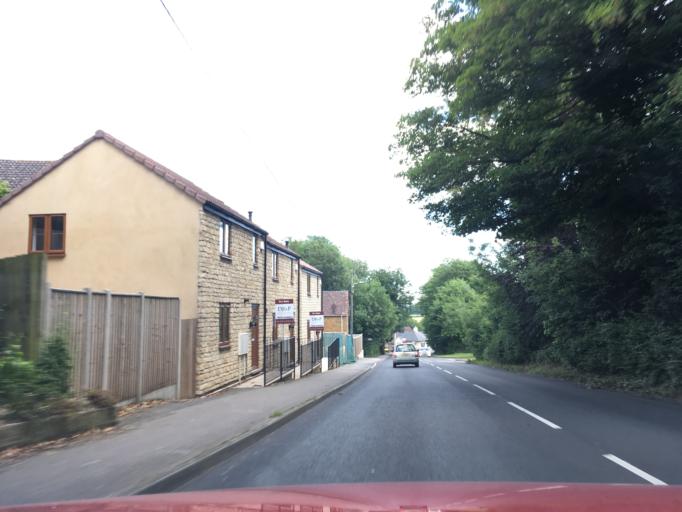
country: GB
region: England
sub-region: Gloucestershire
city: Dursley
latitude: 51.6998
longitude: -2.3662
